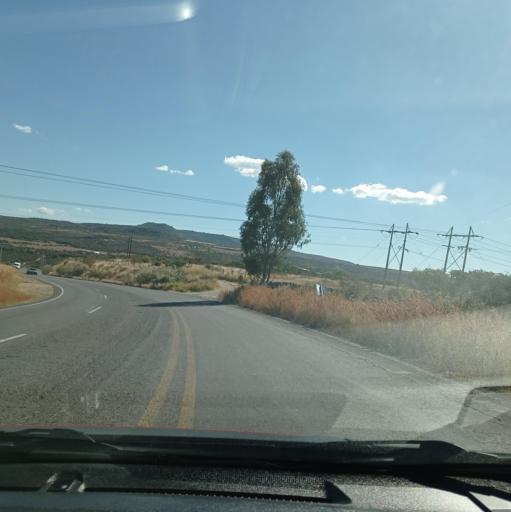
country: MX
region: Jalisco
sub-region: San Julian
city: Colonia Veintitres de Mayo
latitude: 21.0076
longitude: -102.2731
